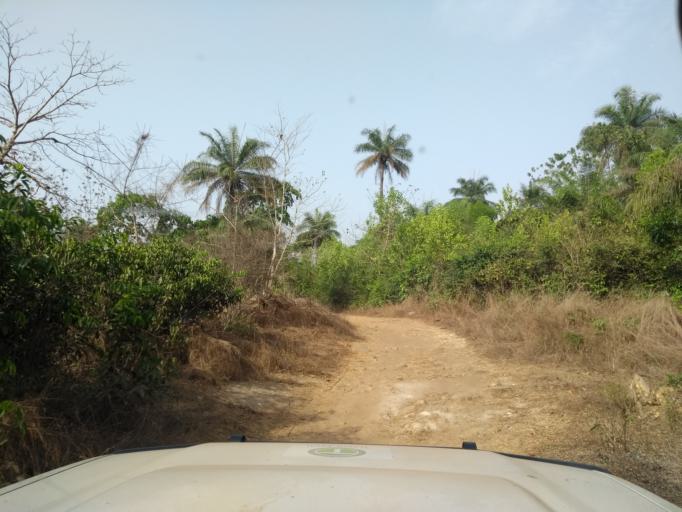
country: GN
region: Kindia
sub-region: Prefecture de Dubreka
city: Dubreka
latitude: 9.8163
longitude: -13.5583
